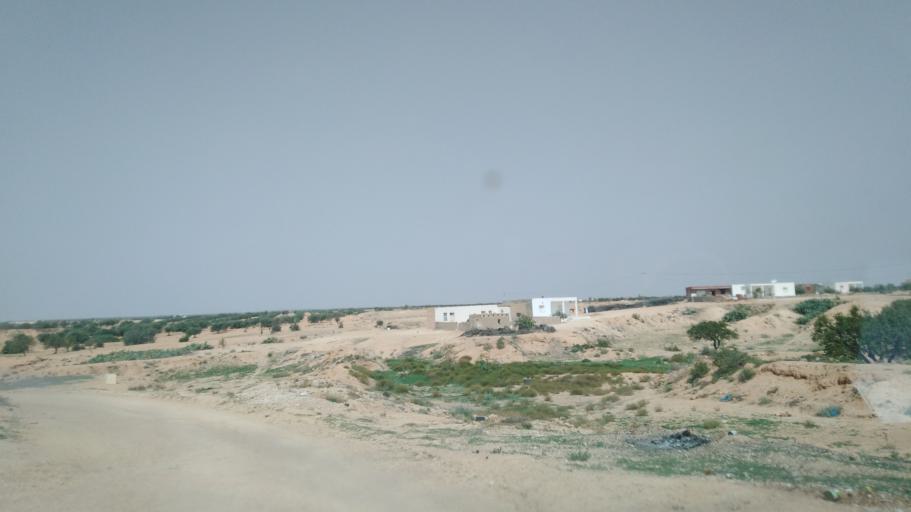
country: TN
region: Safaqis
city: Sfax
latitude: 34.6386
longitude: 10.5691
